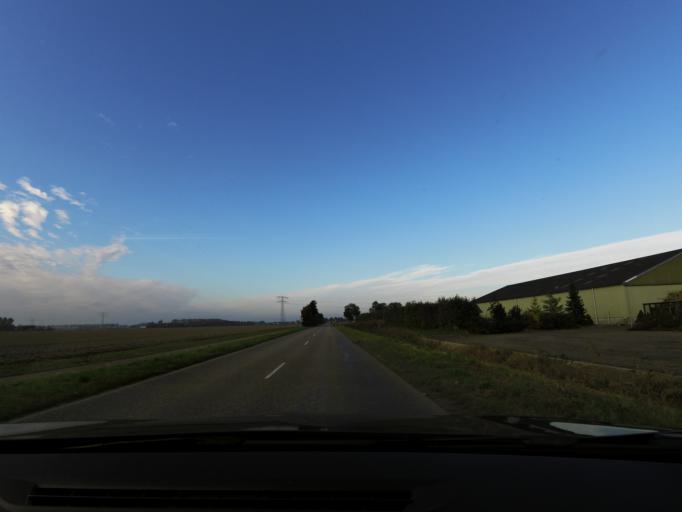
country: NL
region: North Brabant
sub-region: Gemeente Steenbergen
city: Dinteloord
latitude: 51.7017
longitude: 4.2920
